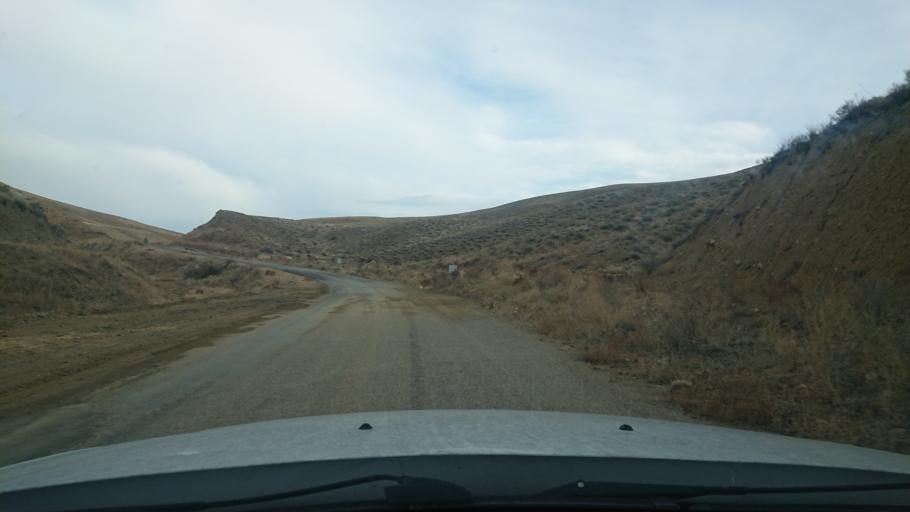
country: TR
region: Aksaray
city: Acipinar
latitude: 38.6253
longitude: 33.7997
